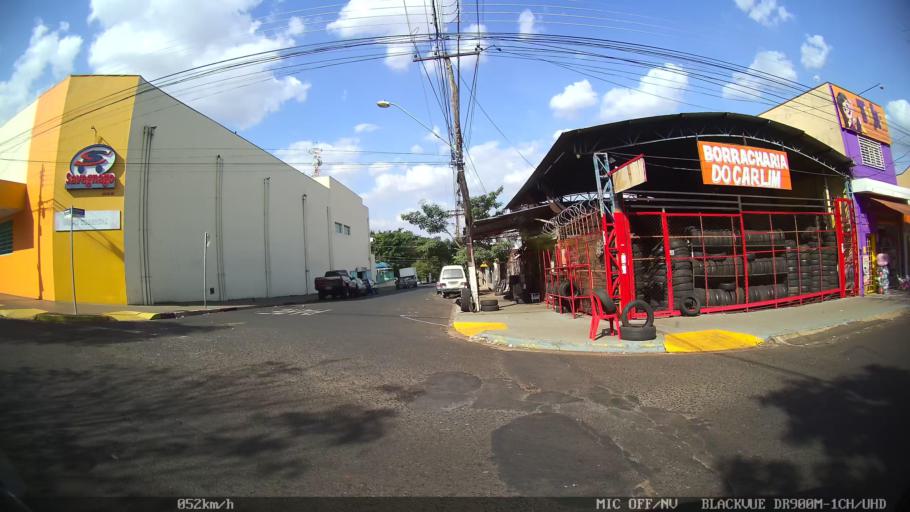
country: BR
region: Sao Paulo
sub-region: Ribeirao Preto
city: Ribeirao Preto
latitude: -21.1905
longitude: -47.8367
